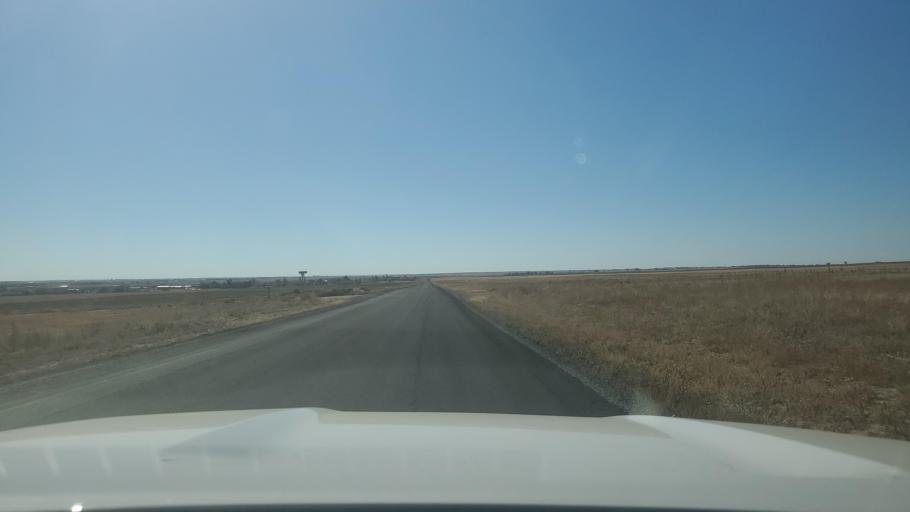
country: US
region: Colorado
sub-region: Adams County
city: Bennett
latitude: 39.7535
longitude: -104.3771
